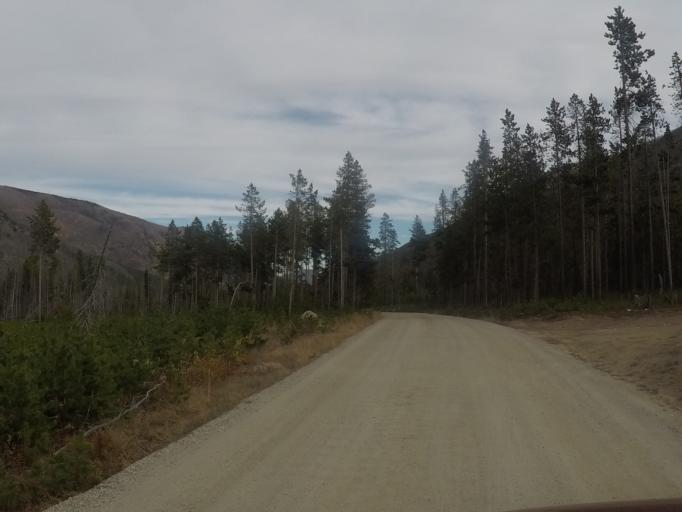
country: US
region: Montana
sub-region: Carbon County
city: Red Lodge
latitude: 45.1730
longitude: -109.4341
